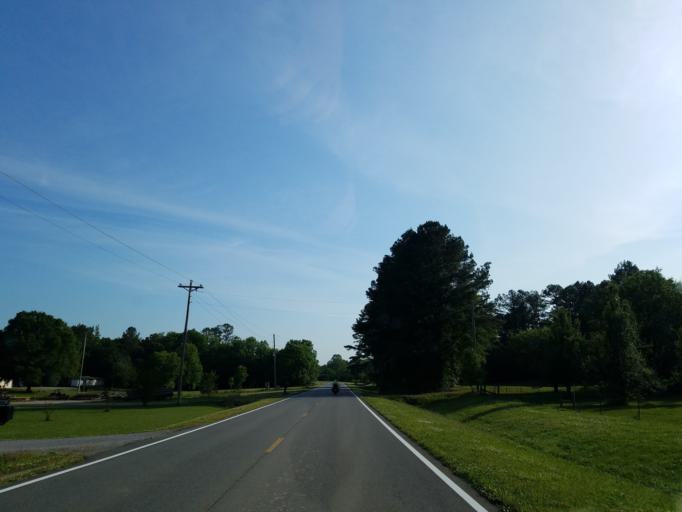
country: US
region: Georgia
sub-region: Chattooga County
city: Trion
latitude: 34.5443
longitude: -85.2026
